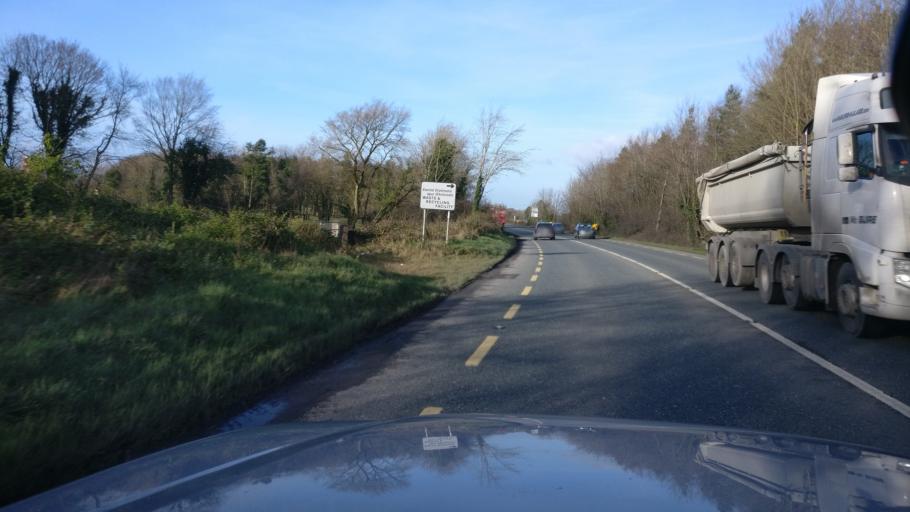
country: IE
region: Leinster
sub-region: Uibh Fhaili
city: Tullamore
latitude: 53.2293
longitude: -7.4754
